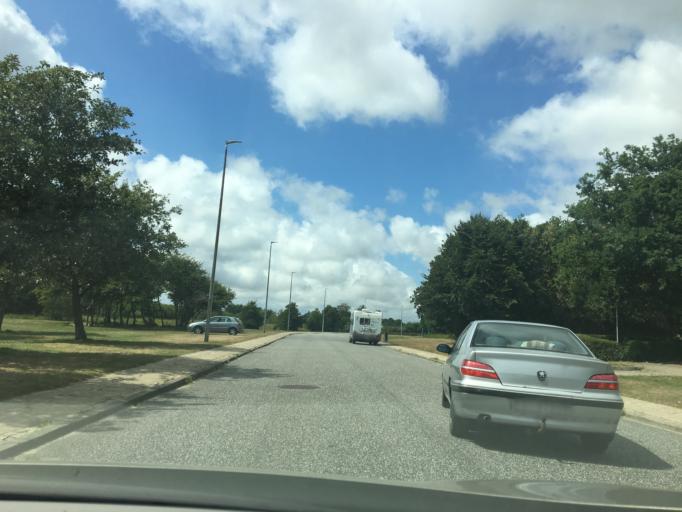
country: DK
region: Central Jutland
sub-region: Ringkobing-Skjern Kommune
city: Tarm
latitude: 55.9084
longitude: 8.5158
